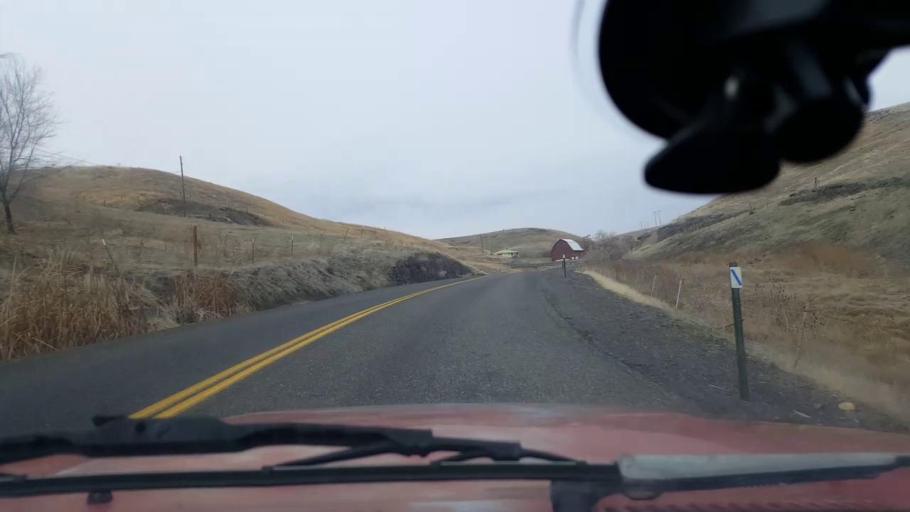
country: US
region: Washington
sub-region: Asotin County
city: Clarkston Heights-Vineland
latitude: 46.3842
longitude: -117.1368
